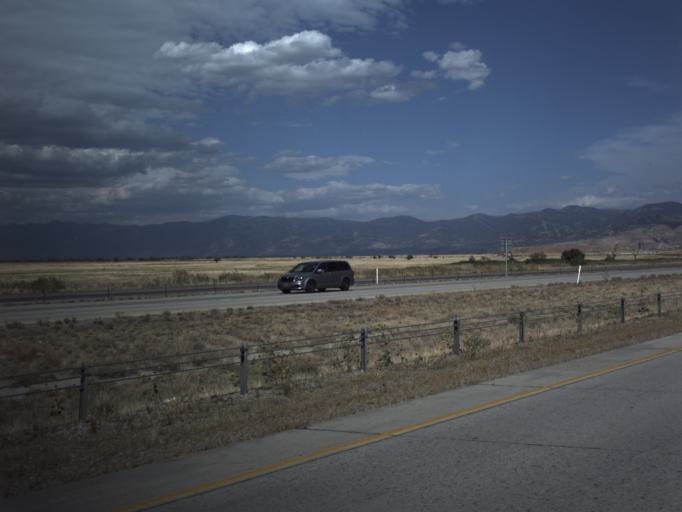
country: US
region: Utah
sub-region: Salt Lake County
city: Magna
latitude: 40.7708
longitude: -112.0814
